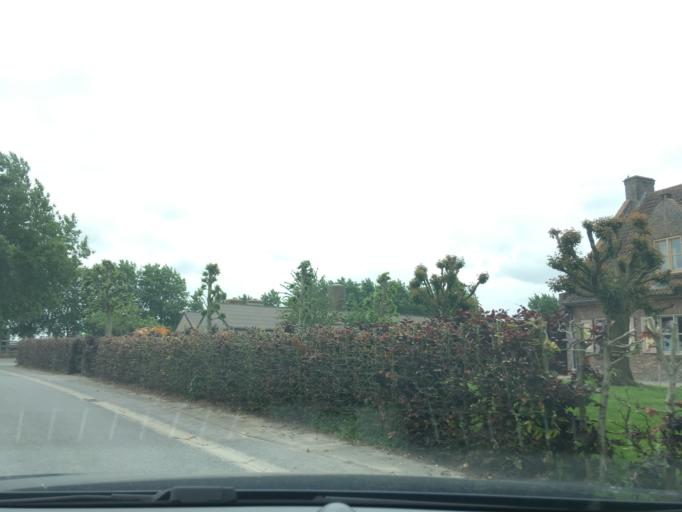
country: BE
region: Flanders
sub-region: Provincie West-Vlaanderen
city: Moorslede
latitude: 50.8399
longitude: 3.0631
